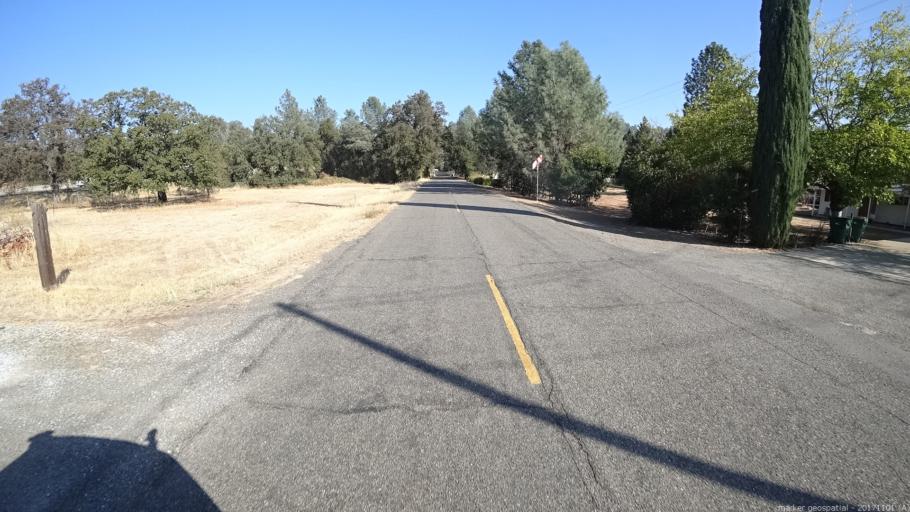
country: US
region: California
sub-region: Shasta County
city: Shasta Lake
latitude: 40.7105
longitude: -122.3332
